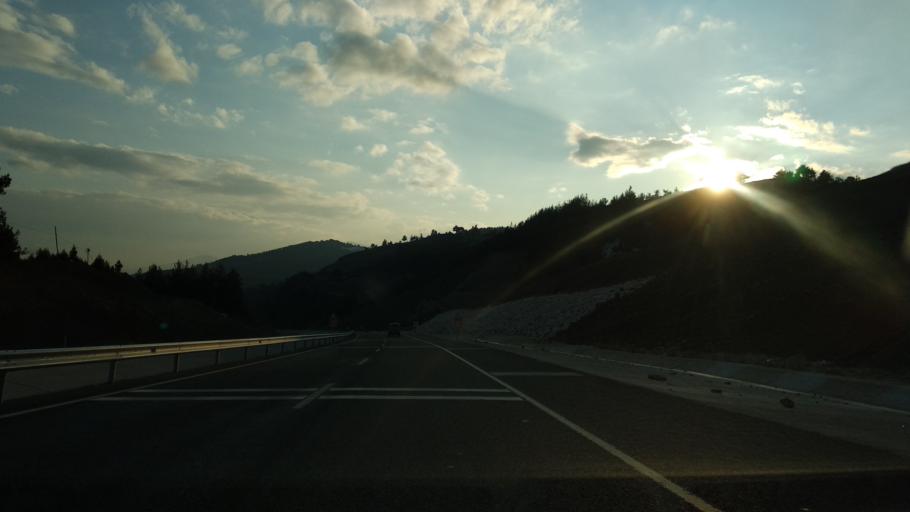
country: TR
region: Kahramanmaras
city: Yenicekale
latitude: 37.7094
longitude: 36.6909
